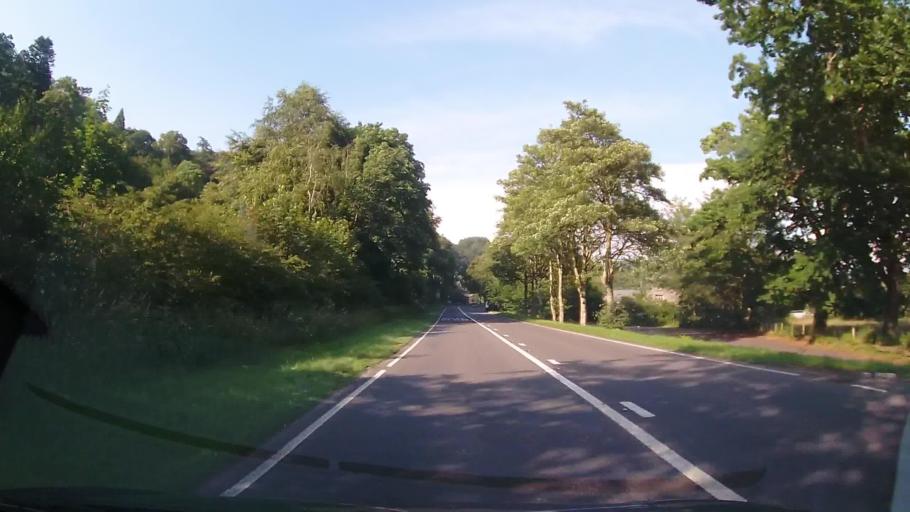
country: GB
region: Wales
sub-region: Gwynedd
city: Maentwrog
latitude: 52.9454
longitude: -3.9997
